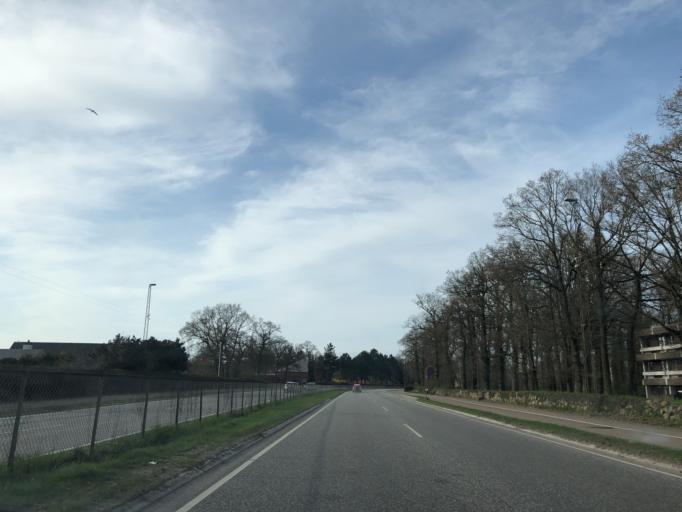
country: DK
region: Zealand
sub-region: Koge Kommune
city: Koge
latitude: 55.4526
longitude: 12.1736
